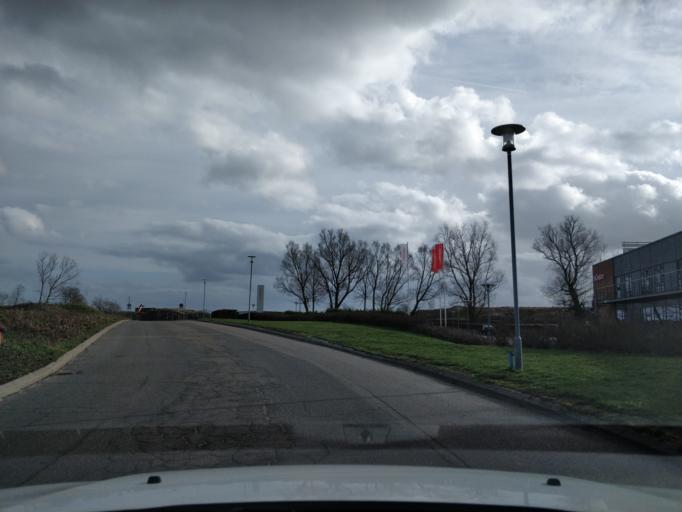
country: DK
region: Capital Region
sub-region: Hoje-Taastrup Kommune
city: Taastrup
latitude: 55.6411
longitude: 12.2617
